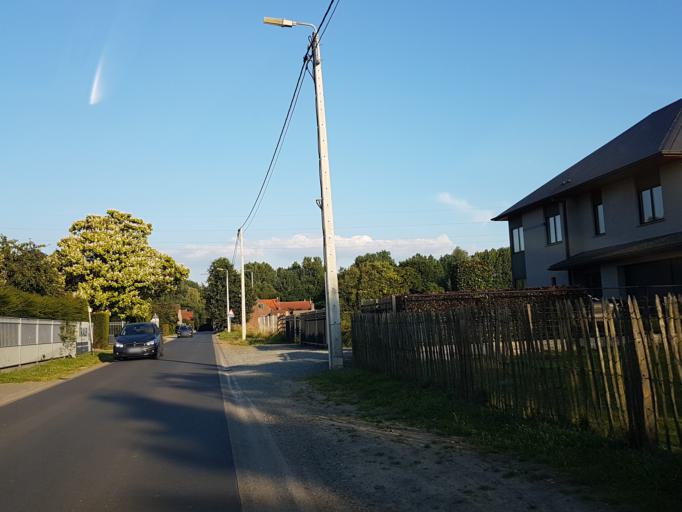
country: BE
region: Flanders
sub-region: Provincie Vlaams-Brabant
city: Opwijk
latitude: 50.9563
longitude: 4.2036
